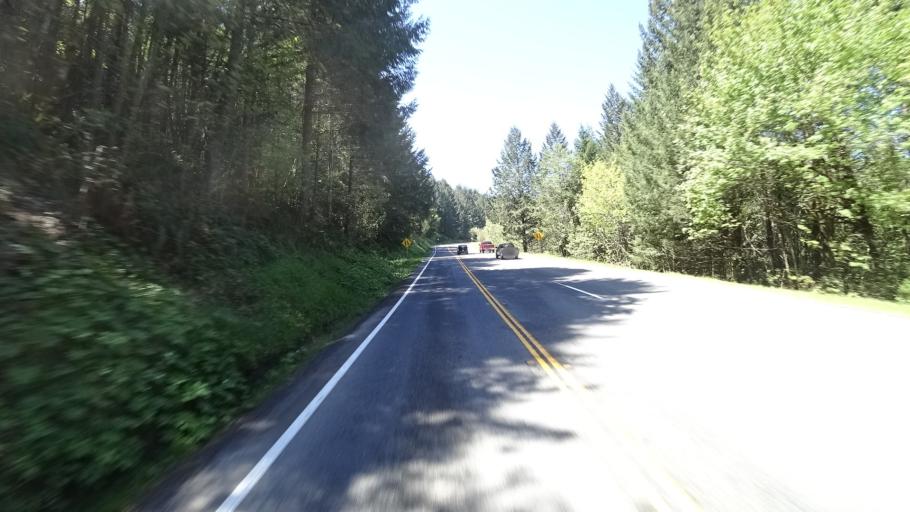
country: US
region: California
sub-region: Humboldt County
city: Blue Lake
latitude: 40.9050
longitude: -123.8165
